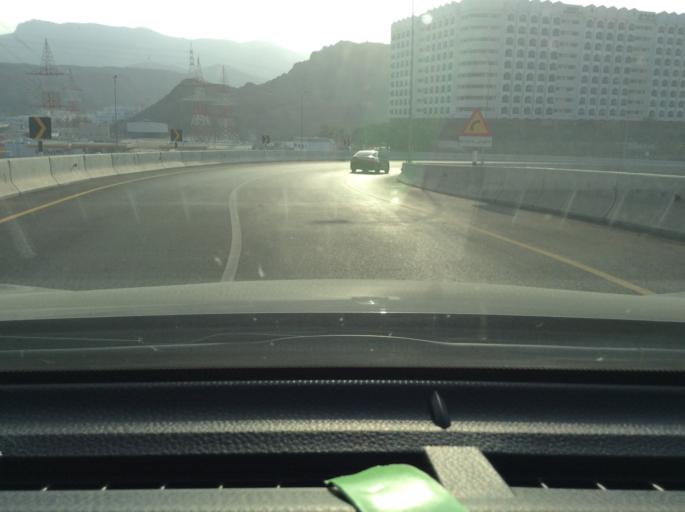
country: OM
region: Muhafazat Masqat
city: Muscat
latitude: 23.5928
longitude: 58.5261
